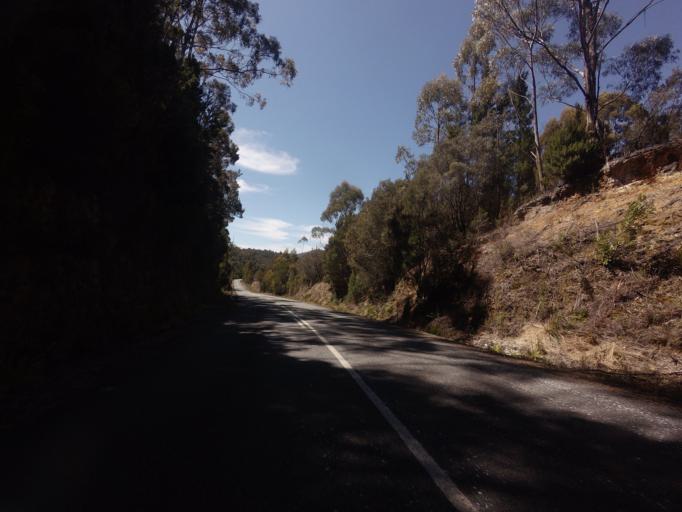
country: AU
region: Tasmania
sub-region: West Coast
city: Queenstown
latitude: -42.7794
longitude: 146.0359
